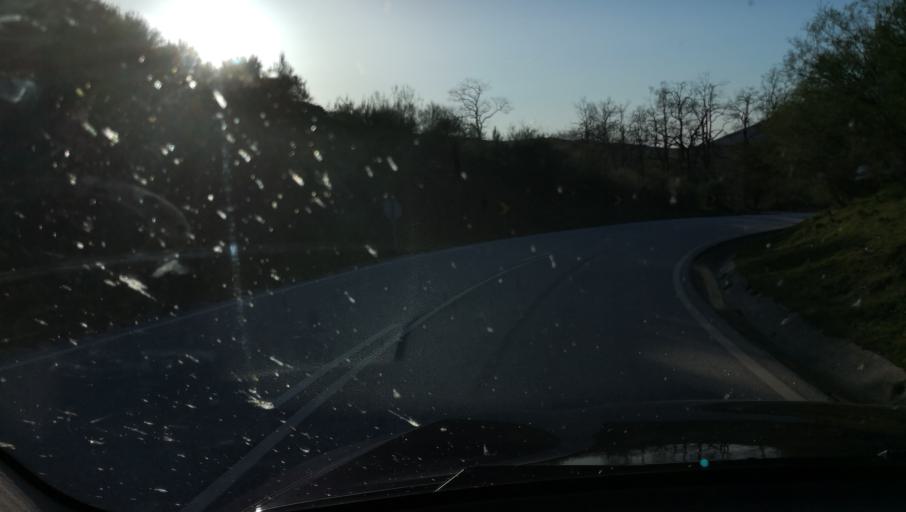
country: PT
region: Vila Real
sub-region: Vila Real
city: Vila Real
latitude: 41.3648
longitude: -7.8003
